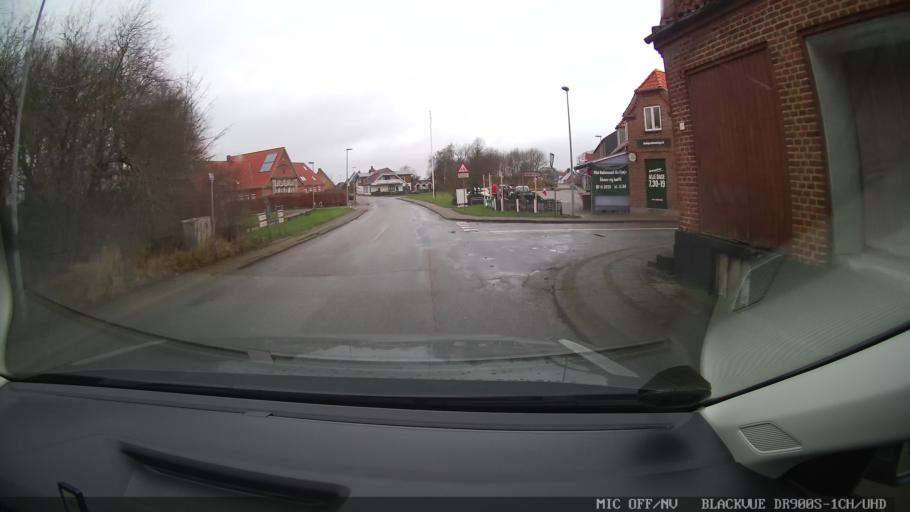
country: DK
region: Central Jutland
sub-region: Viborg Kommune
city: Karup
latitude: 56.3574
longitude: 9.2953
